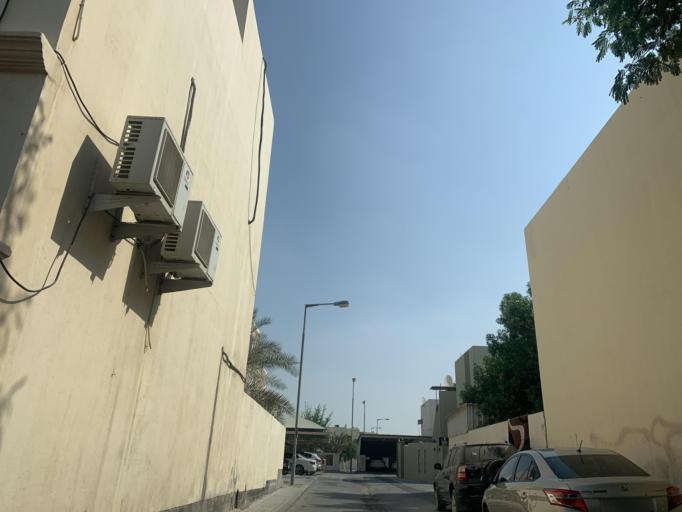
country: BH
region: Central Governorate
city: Madinat Hamad
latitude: 26.1280
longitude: 50.4954
